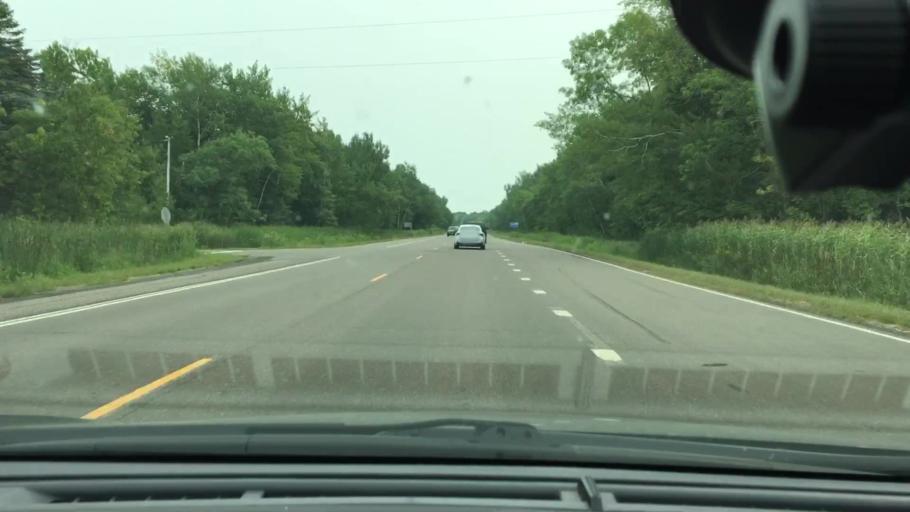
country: US
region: Minnesota
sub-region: Mille Lacs County
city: Vineland
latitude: 46.1516
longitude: -93.7447
